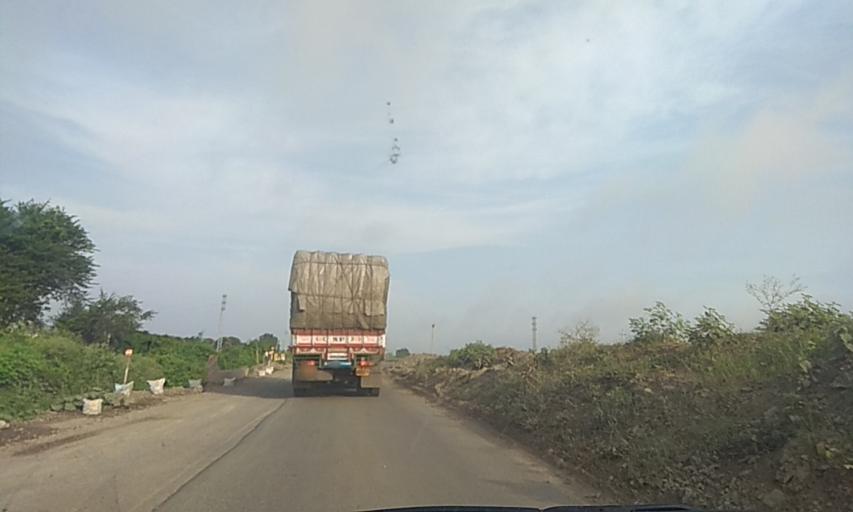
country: IN
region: Karnataka
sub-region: Haveri
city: Byadgi
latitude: 14.7210
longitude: 75.4793
